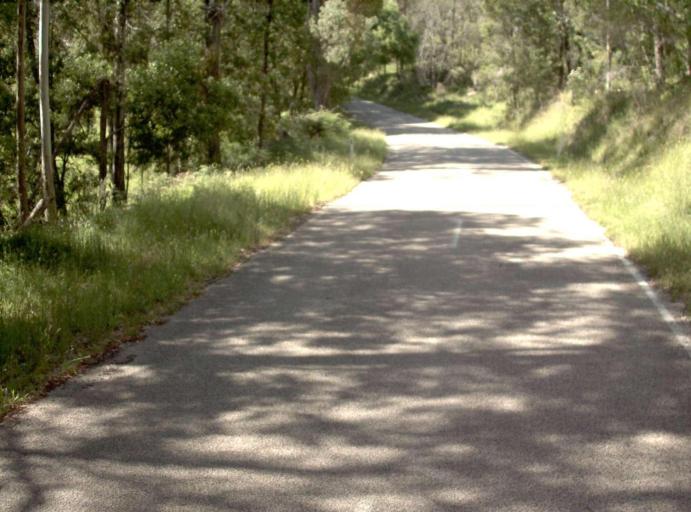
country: AU
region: New South Wales
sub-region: Bombala
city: Bombala
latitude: -37.3404
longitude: 148.6982
